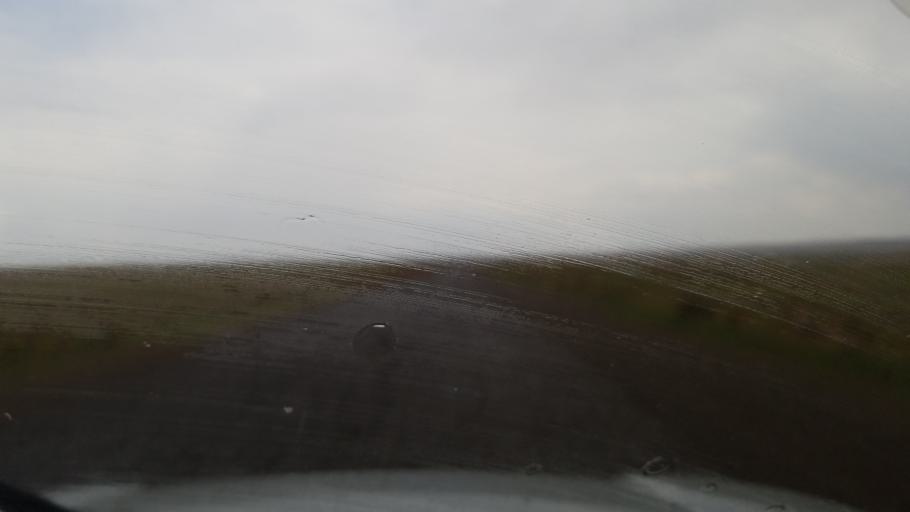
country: TM
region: Mary
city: Serhetabat
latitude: 35.8799
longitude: 62.6203
